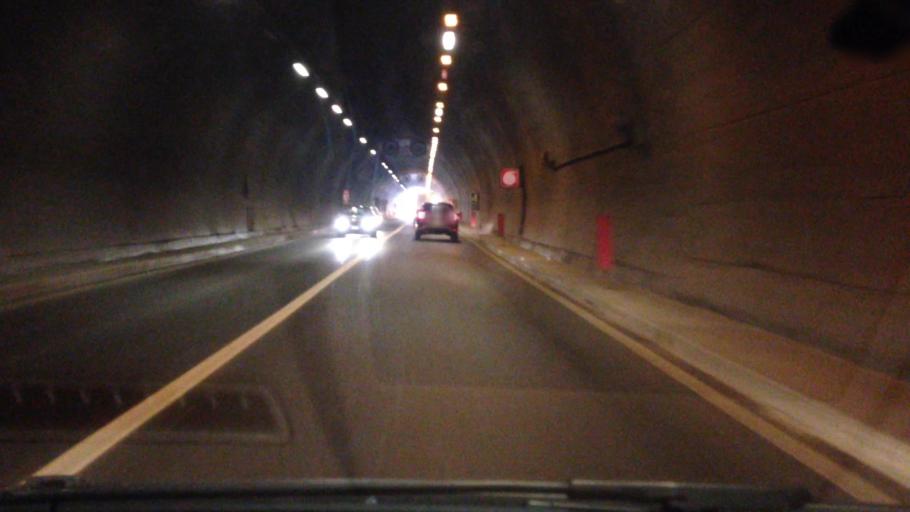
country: IT
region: Piedmont
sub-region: Provincia di Asti
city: Piano-Molini d'Isola
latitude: 44.8380
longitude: 8.1972
